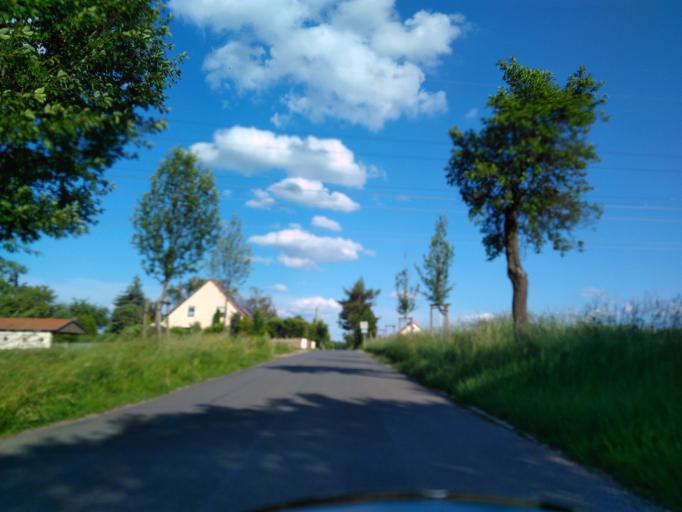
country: DE
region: Thuringia
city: Kromsdorf
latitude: 50.9975
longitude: 11.3519
